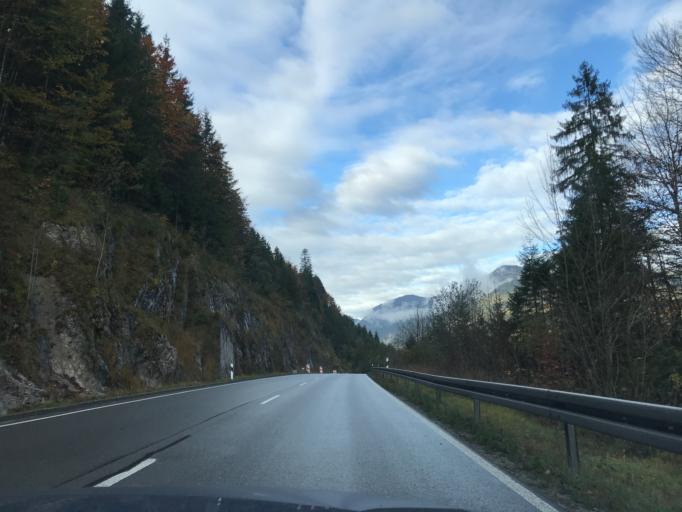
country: DE
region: Bavaria
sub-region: Upper Bavaria
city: Jachenau
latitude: 47.5604
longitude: 11.5076
